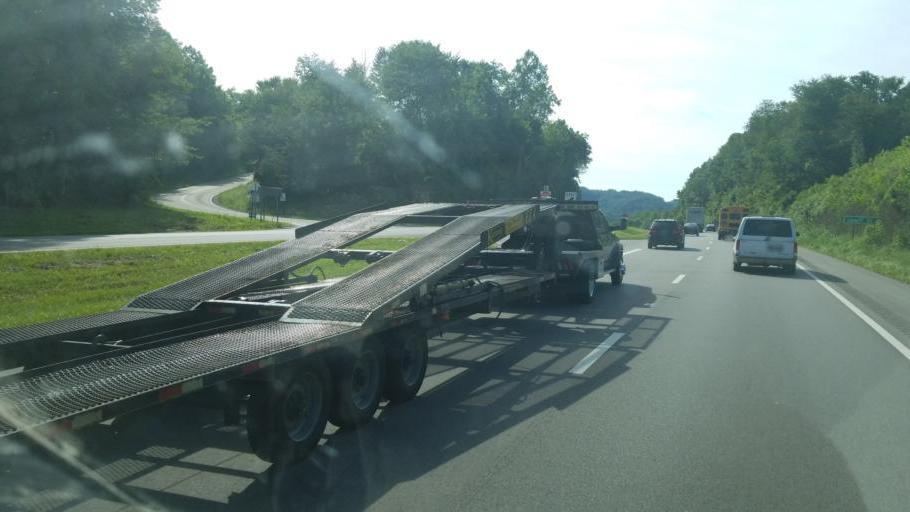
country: US
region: Ohio
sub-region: Fairfield County
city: Geneva
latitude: 39.5849
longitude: -82.5273
